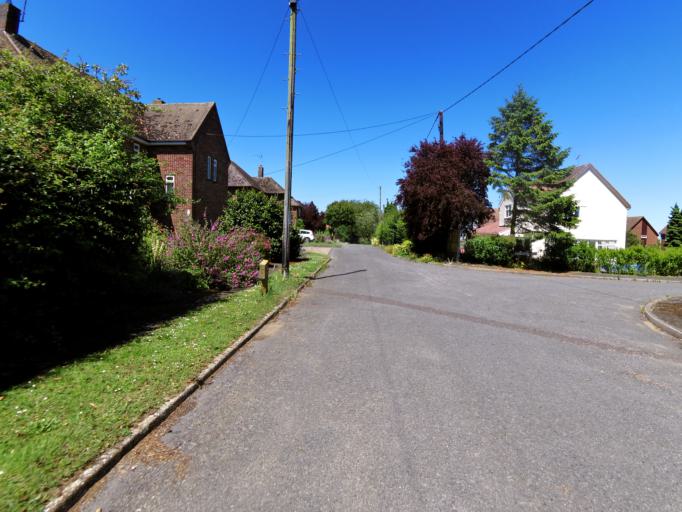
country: GB
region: England
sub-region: Suffolk
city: Felixstowe
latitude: 52.0262
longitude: 1.4171
